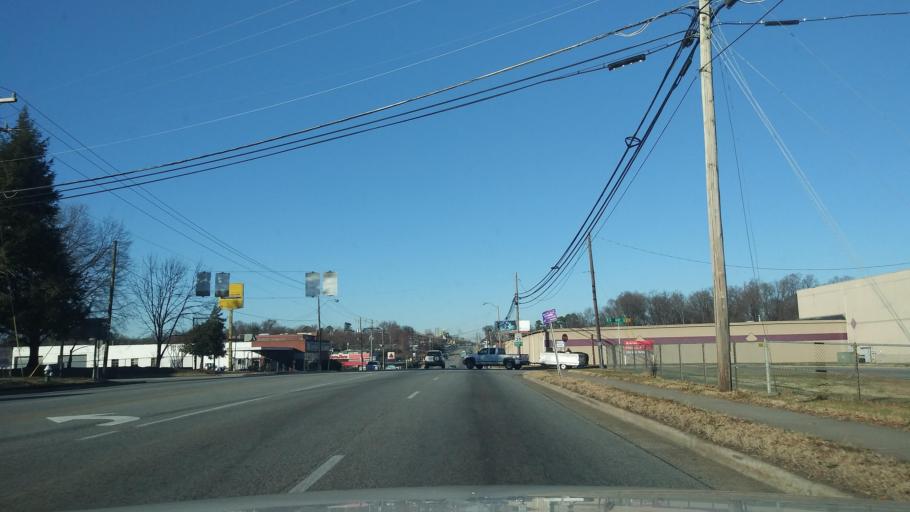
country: US
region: North Carolina
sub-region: Guilford County
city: Greensboro
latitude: 36.0371
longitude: -79.7914
